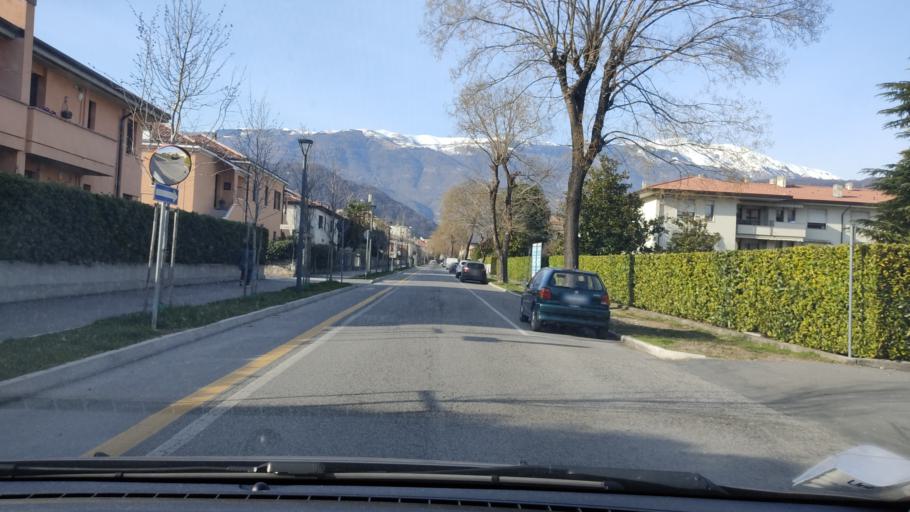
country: IT
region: Veneto
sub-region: Provincia di Treviso
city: Vittorio Veneto
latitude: 45.9823
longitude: 12.3012
